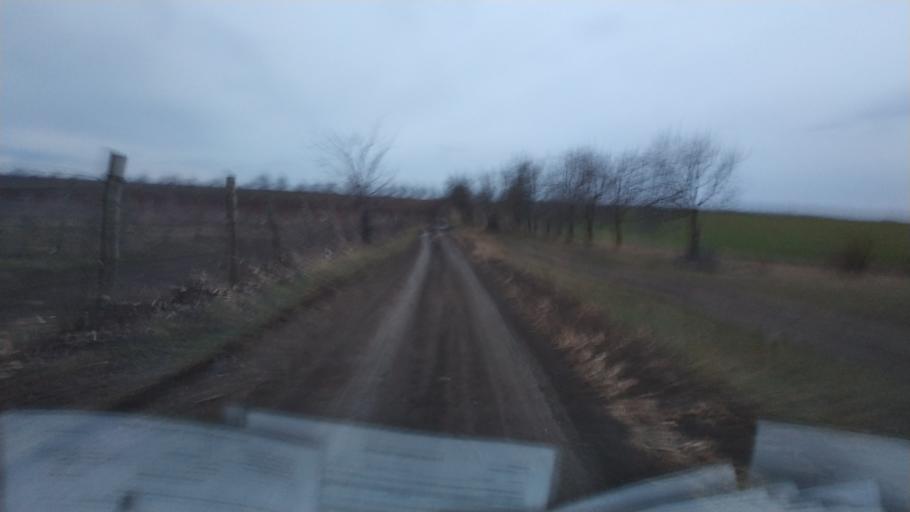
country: MD
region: Causeni
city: Causeni
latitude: 46.5061
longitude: 29.4209
